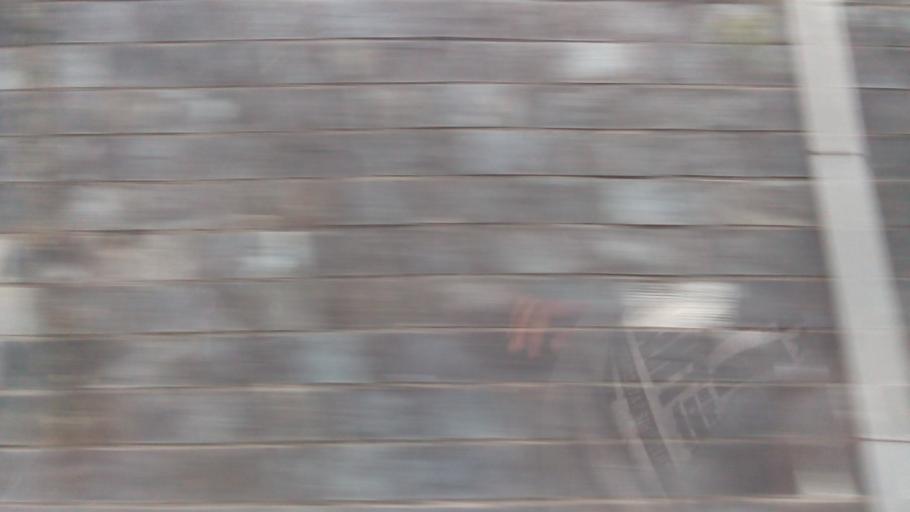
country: TW
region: Taiwan
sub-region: Hualien
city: Hualian
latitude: 24.3484
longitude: 121.3215
